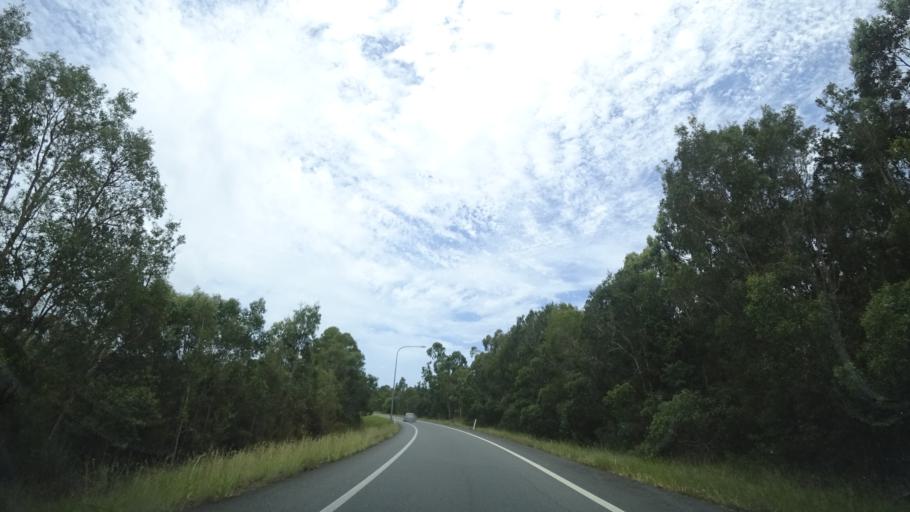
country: AU
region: Queensland
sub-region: Sunshine Coast
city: Mooloolaba
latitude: -26.6947
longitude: 153.1091
